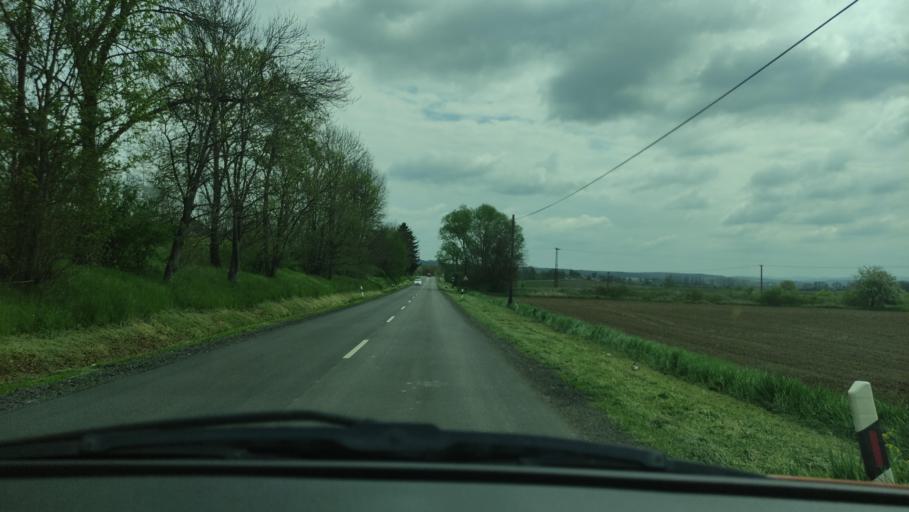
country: HU
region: Baranya
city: Sasd
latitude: 46.2656
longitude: 18.0816
